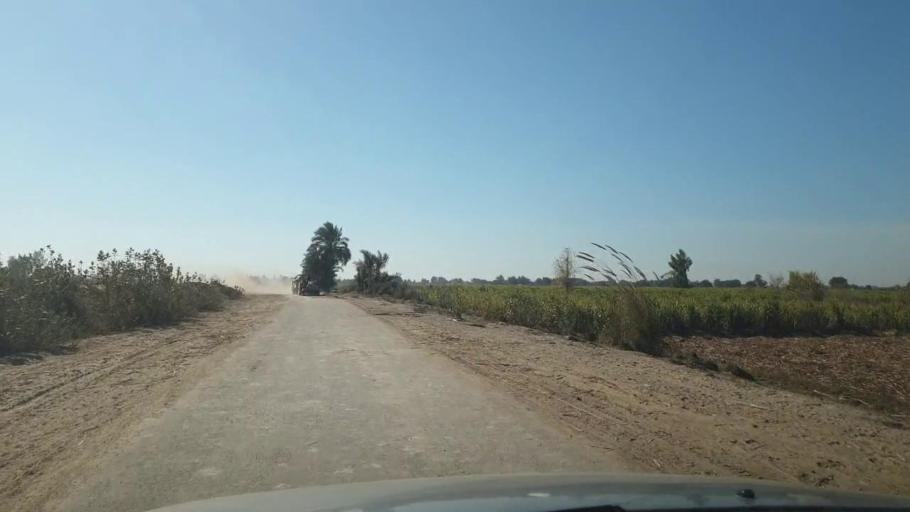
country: PK
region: Sindh
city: Ghotki
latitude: 28.0224
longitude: 69.2684
